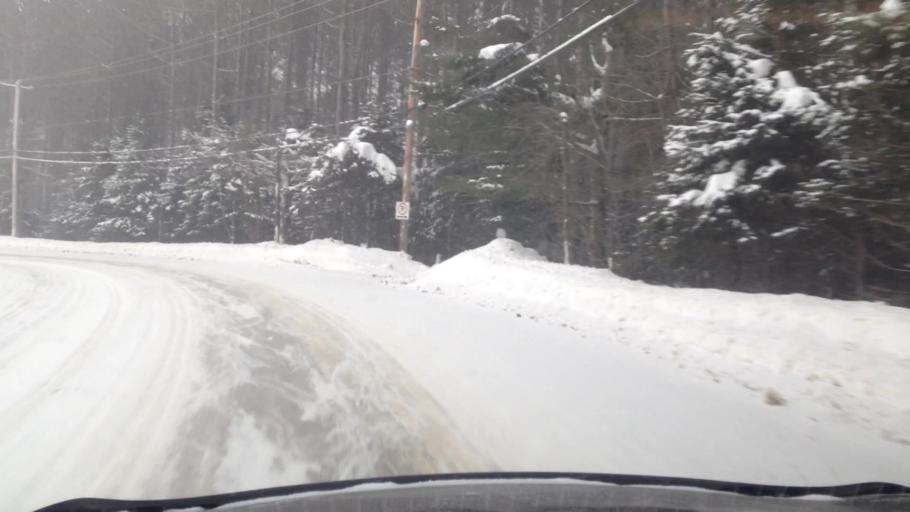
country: CA
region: Quebec
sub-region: Laurentides
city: Mont-Tremblant
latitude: 45.9682
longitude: -74.6283
